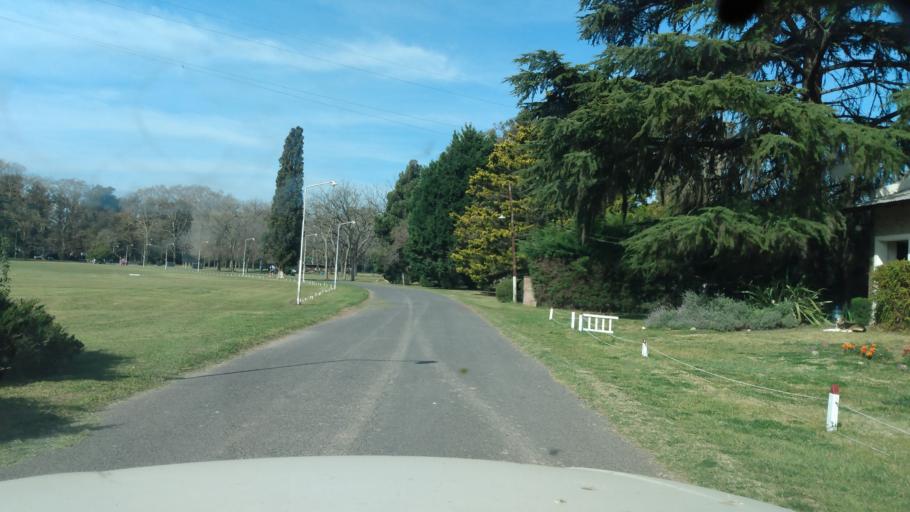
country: AR
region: Buenos Aires
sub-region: Partido de Lujan
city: Lujan
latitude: -34.5926
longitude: -59.1842
